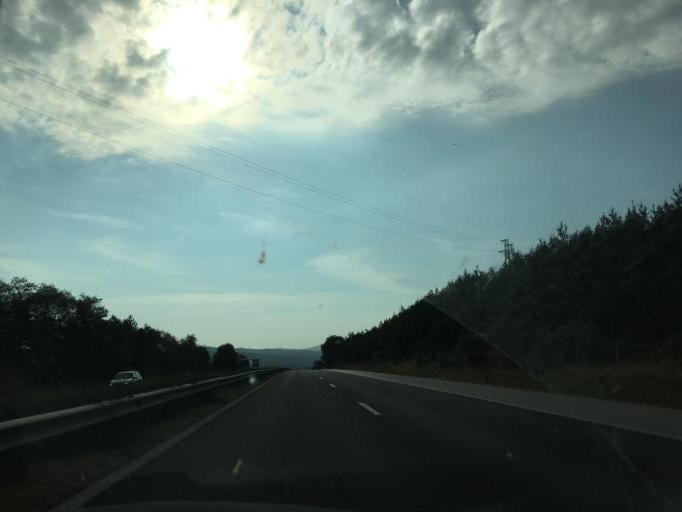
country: BG
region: Sofiya
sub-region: Obshtina Gorna Malina
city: Gorna Malina
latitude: 42.5487
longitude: 23.7060
